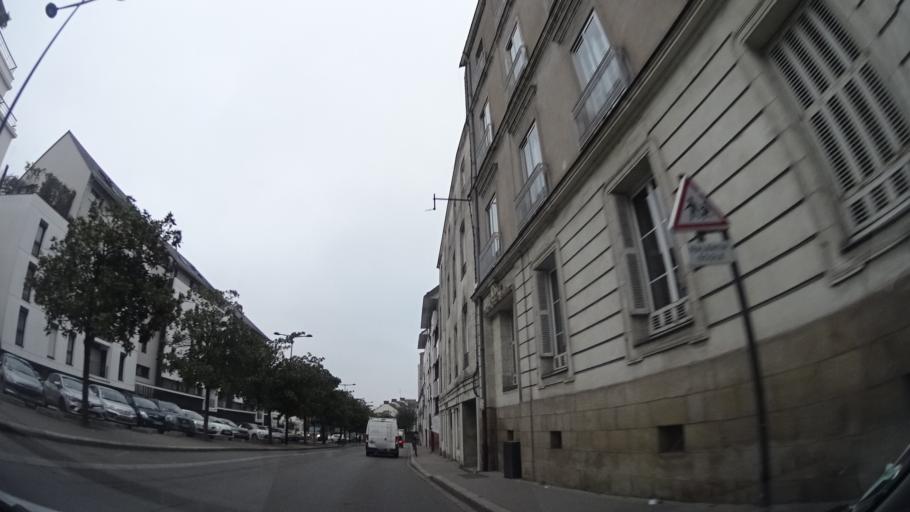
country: FR
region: Pays de la Loire
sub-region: Departement de la Loire-Atlantique
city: Nantes
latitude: 47.2144
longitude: -1.5690
